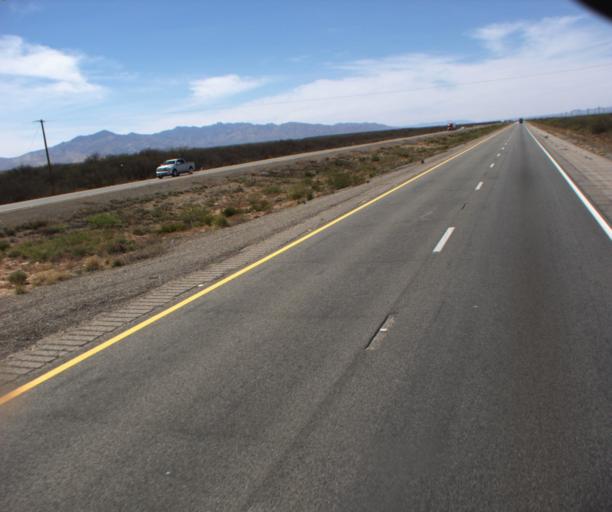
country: US
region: Arizona
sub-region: Cochise County
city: Willcox
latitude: 32.2822
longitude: -109.2870
